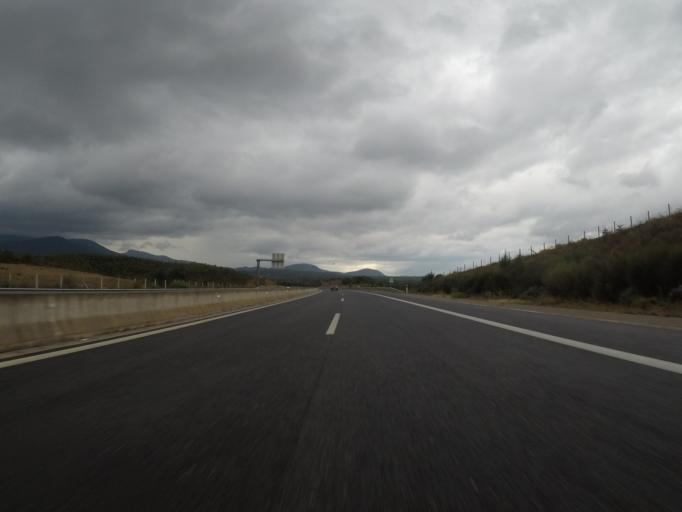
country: GR
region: Peloponnese
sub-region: Nomos Arkadias
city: Megalopoli
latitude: 37.3578
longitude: 22.1251
